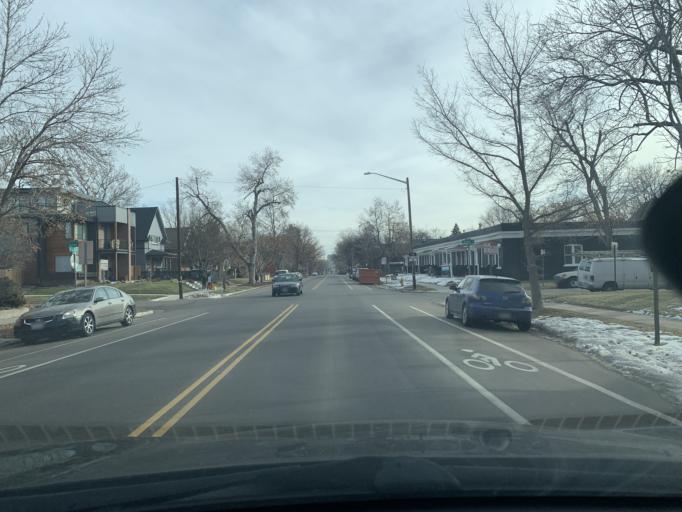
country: US
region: Colorado
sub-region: Jefferson County
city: Edgewater
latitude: 39.7512
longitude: -105.0319
